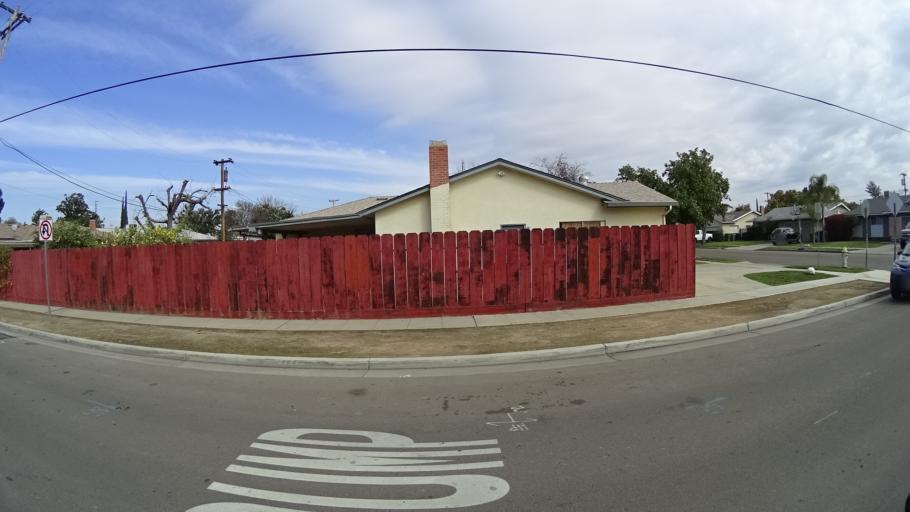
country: US
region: California
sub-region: Fresno County
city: Fresno
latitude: 36.8122
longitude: -119.7705
